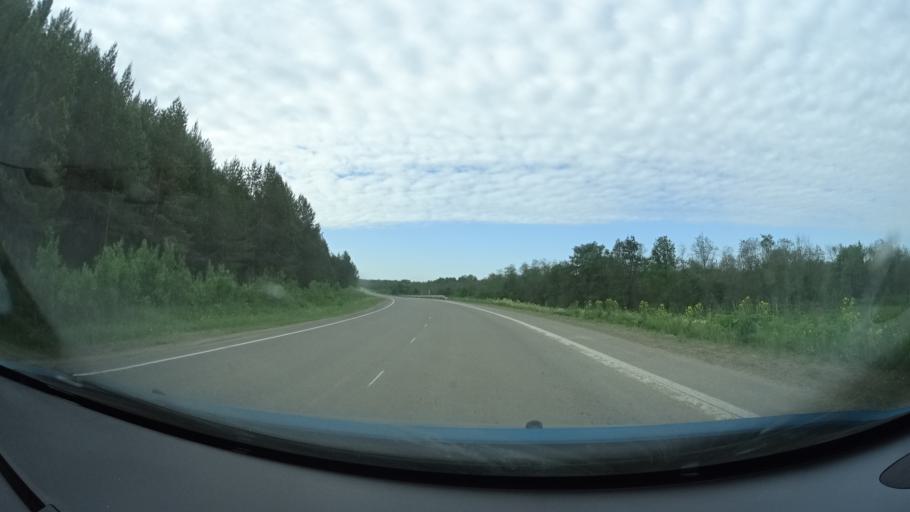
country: RU
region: Perm
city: Kuyeda
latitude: 56.5220
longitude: 55.6261
